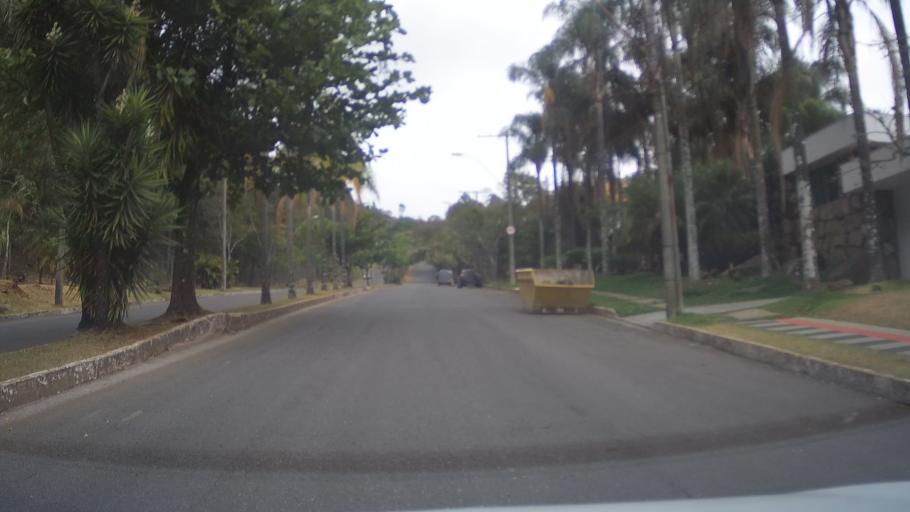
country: BR
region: Minas Gerais
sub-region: Belo Horizonte
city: Belo Horizonte
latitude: -19.9601
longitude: -43.9159
